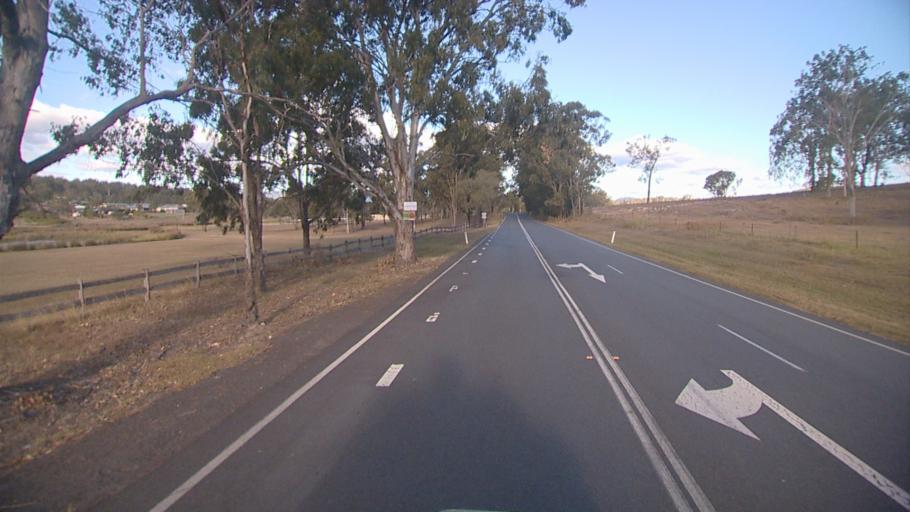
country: AU
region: Queensland
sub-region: Logan
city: Cedar Vale
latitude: -27.8774
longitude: 153.0682
